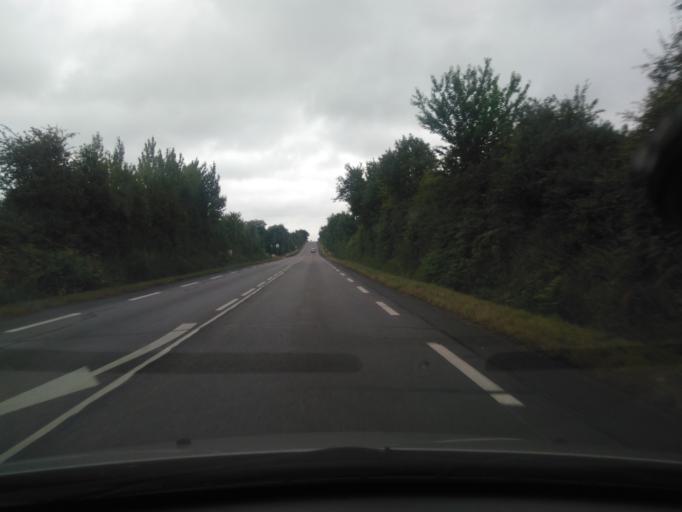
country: FR
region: Pays de la Loire
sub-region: Departement de la Vendee
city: Saint-Florent-des-Bois
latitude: 46.5864
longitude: -1.3047
